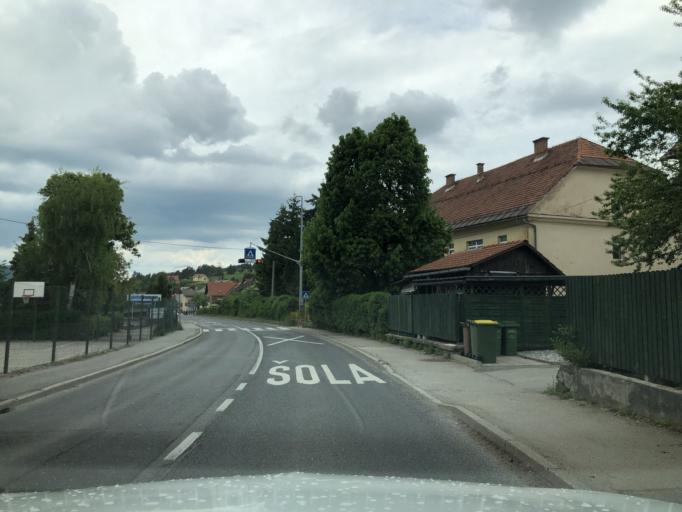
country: SI
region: Cerknica
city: Rakek
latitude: 45.8111
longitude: 14.3235
